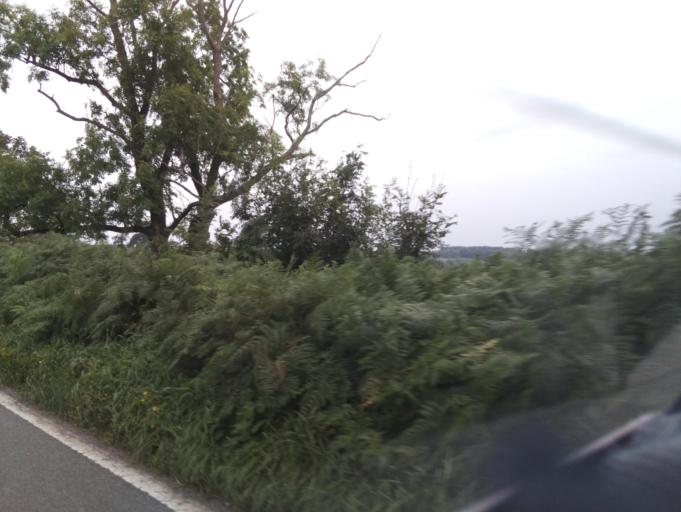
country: GB
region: England
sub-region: Derbyshire
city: Wirksworth
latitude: 53.0173
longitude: -1.5900
